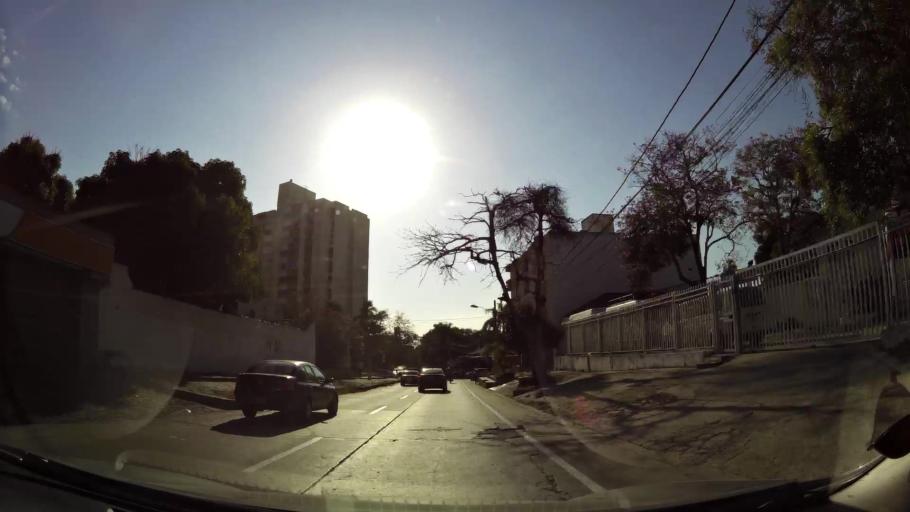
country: CO
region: Atlantico
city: Barranquilla
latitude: 10.9948
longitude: -74.7993
